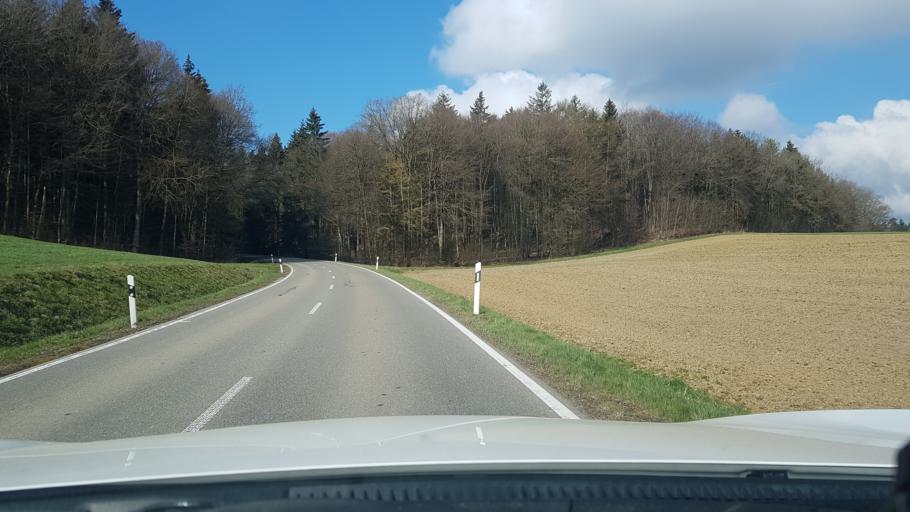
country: DE
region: Baden-Wuerttemberg
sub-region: Tuebingen Region
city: Schwendi
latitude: 48.1519
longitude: 9.9369
